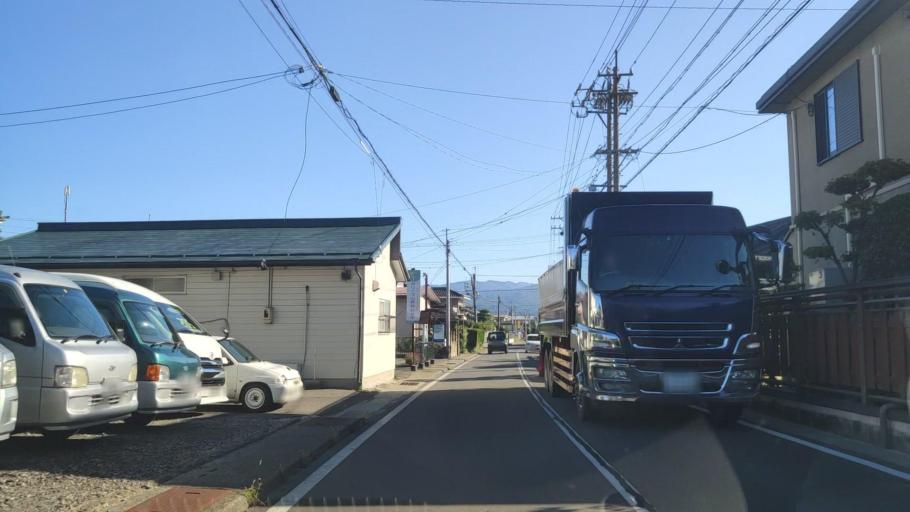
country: JP
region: Nagano
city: Okaya
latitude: 36.0553
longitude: 138.0564
